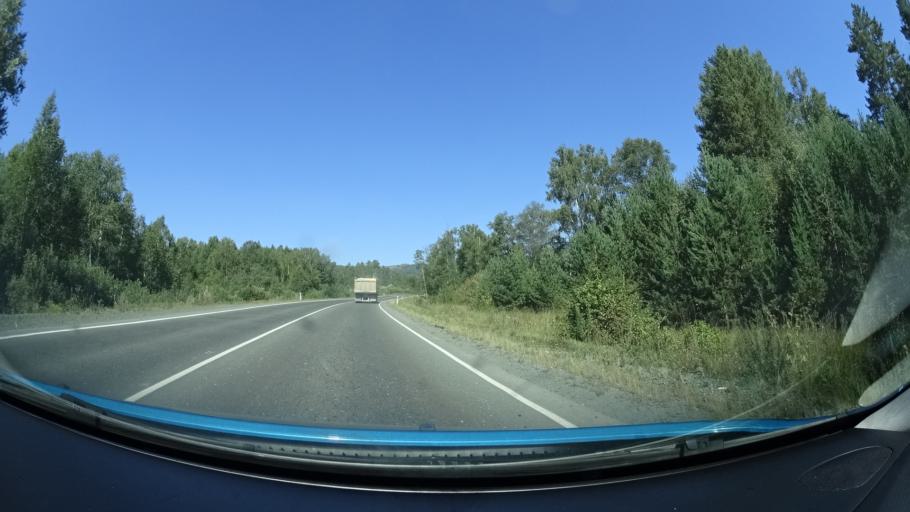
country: RU
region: Bashkortostan
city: Abzakovo
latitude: 53.8628
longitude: 58.5451
